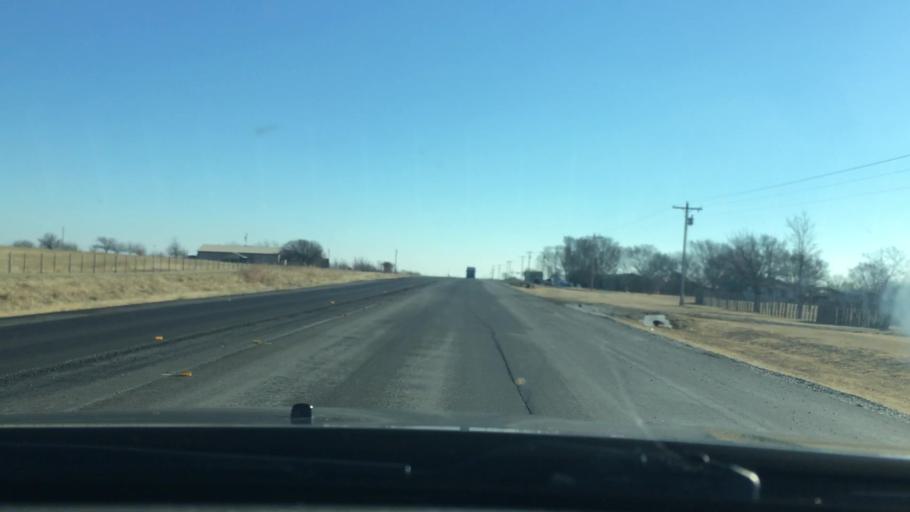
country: US
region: Oklahoma
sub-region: Love County
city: Marietta
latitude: 33.9404
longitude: -97.1596
